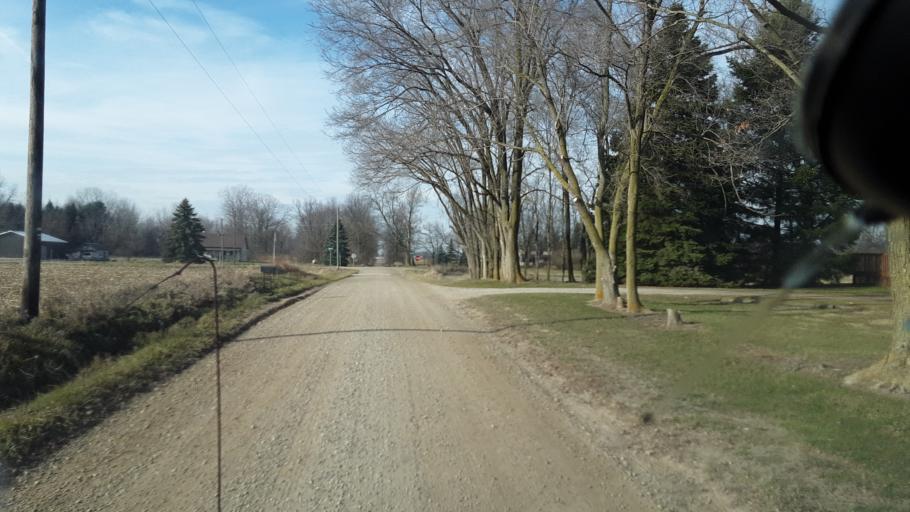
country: US
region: Ohio
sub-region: Defiance County
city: Hicksville
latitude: 41.2705
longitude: -84.8268
